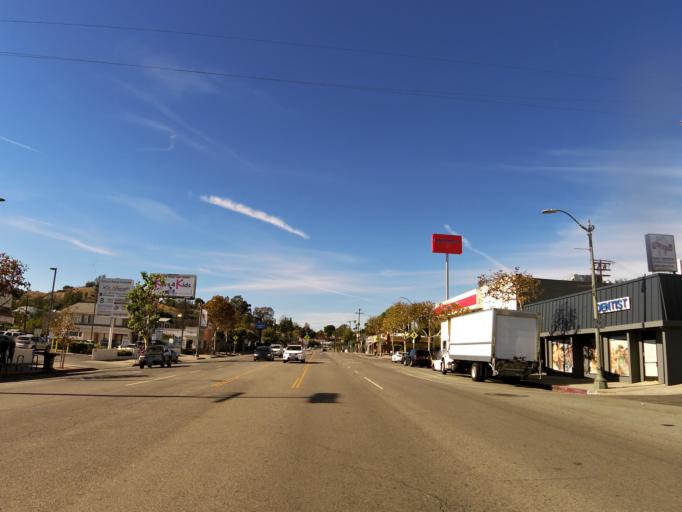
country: US
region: California
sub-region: Los Angeles County
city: Glendale
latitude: 34.1393
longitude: -118.2150
